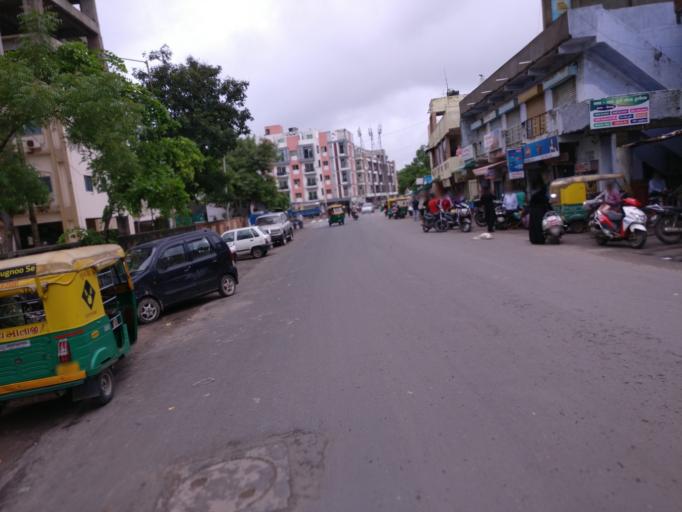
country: IN
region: Gujarat
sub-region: Ahmadabad
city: Sarkhej
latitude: 22.9926
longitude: 72.5195
